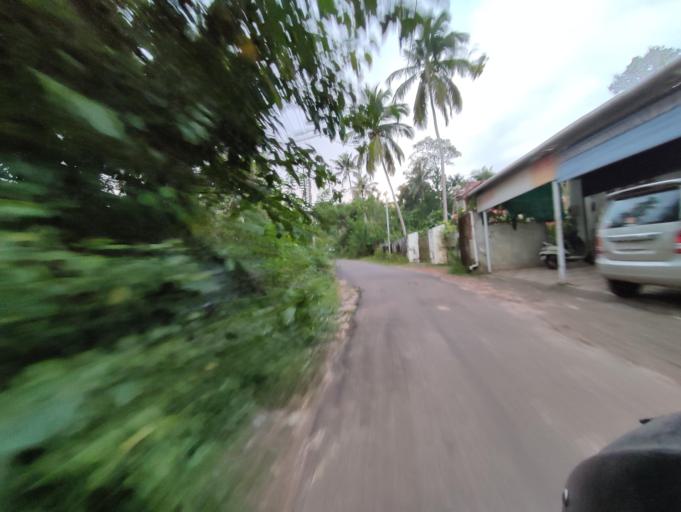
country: IN
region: Kerala
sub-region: Alappuzha
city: Vayalar
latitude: 9.6923
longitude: 76.3316
